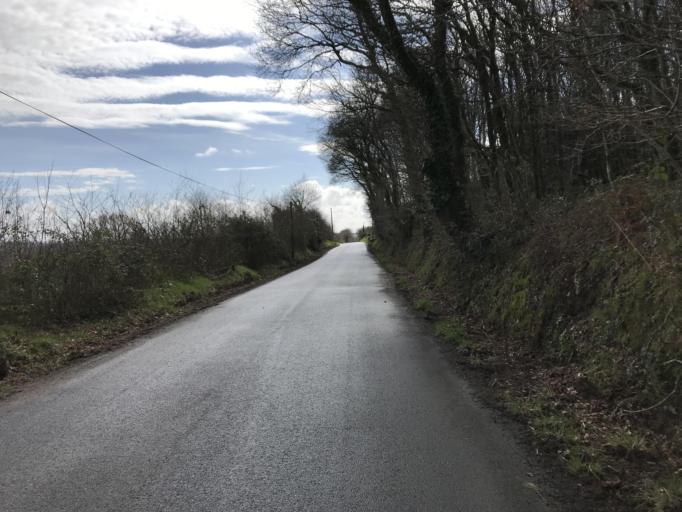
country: FR
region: Brittany
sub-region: Departement du Finistere
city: Daoulas
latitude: 48.3694
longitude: -4.2679
